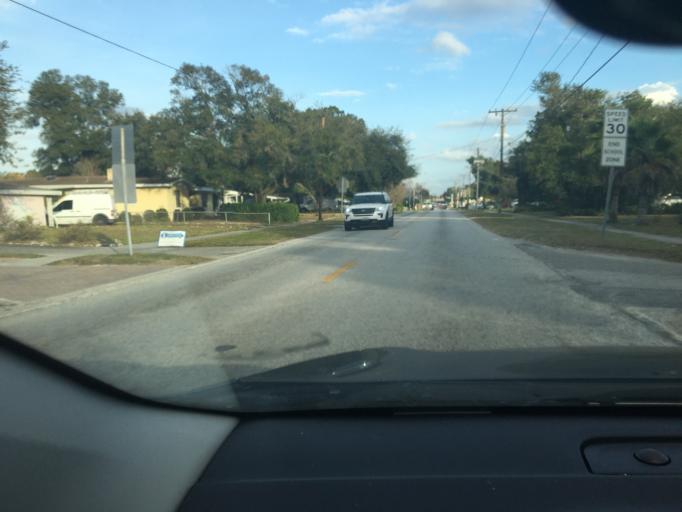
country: US
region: Florida
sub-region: Hillsborough County
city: Carrollwood
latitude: 28.0400
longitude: -82.4632
